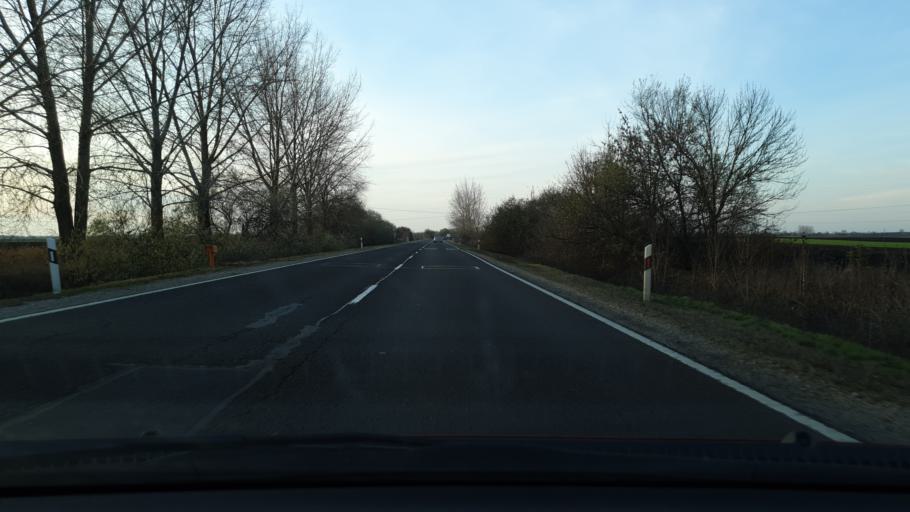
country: HU
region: Jasz-Nagykun-Szolnok
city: Toszeg
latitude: 47.1585
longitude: 20.1144
